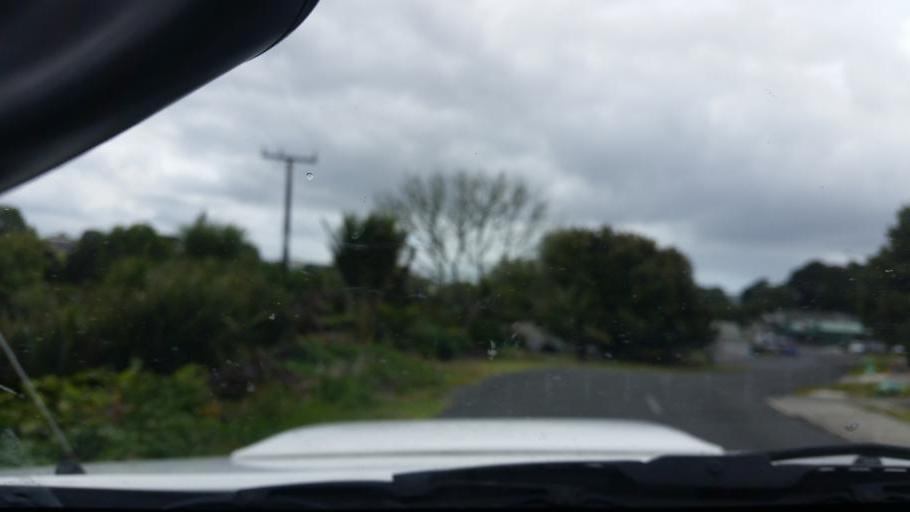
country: NZ
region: Northland
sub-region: Whangarei
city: Ruakaka
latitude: -36.1130
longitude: 174.3509
